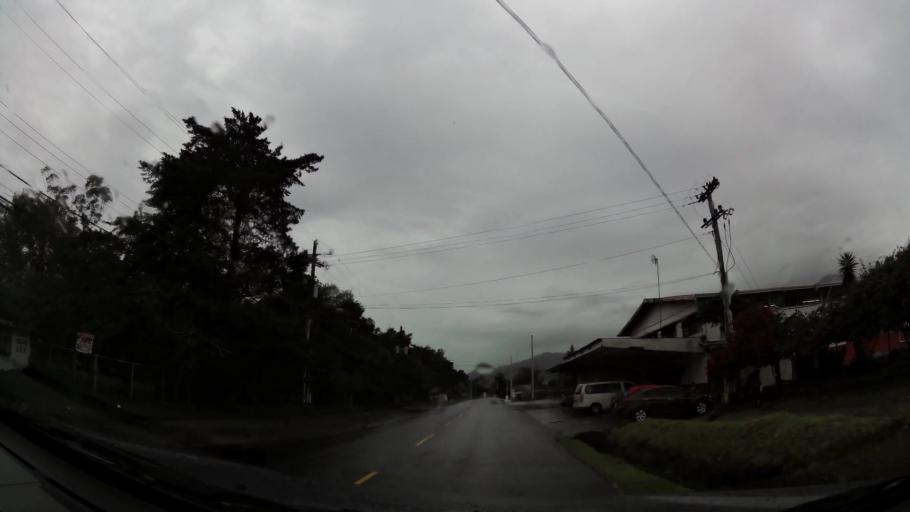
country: PA
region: Chiriqui
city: Volcan
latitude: 8.7883
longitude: -82.6527
